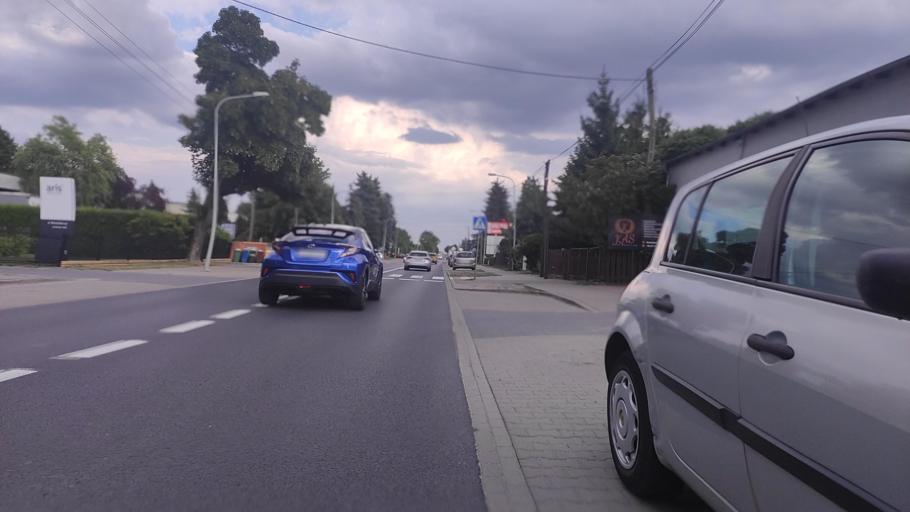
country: PL
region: Greater Poland Voivodeship
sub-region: Powiat poznanski
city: Swarzedz
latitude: 52.4081
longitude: 17.0967
